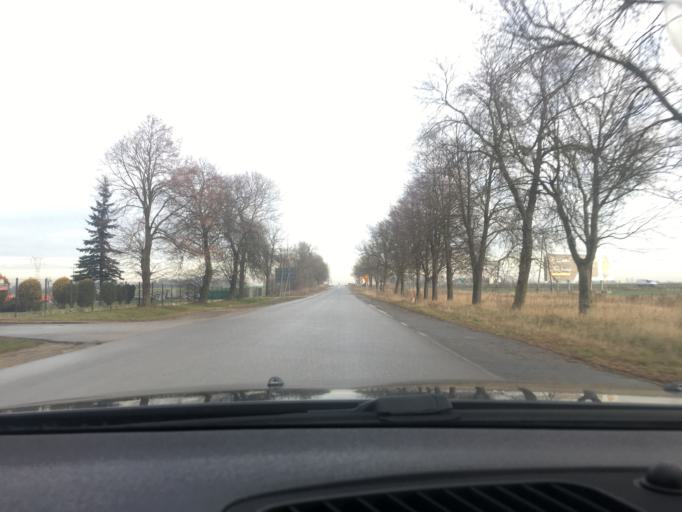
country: PL
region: Swietokrzyskie
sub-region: Powiat jedrzejowski
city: Jedrzejow
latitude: 50.6519
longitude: 20.3203
